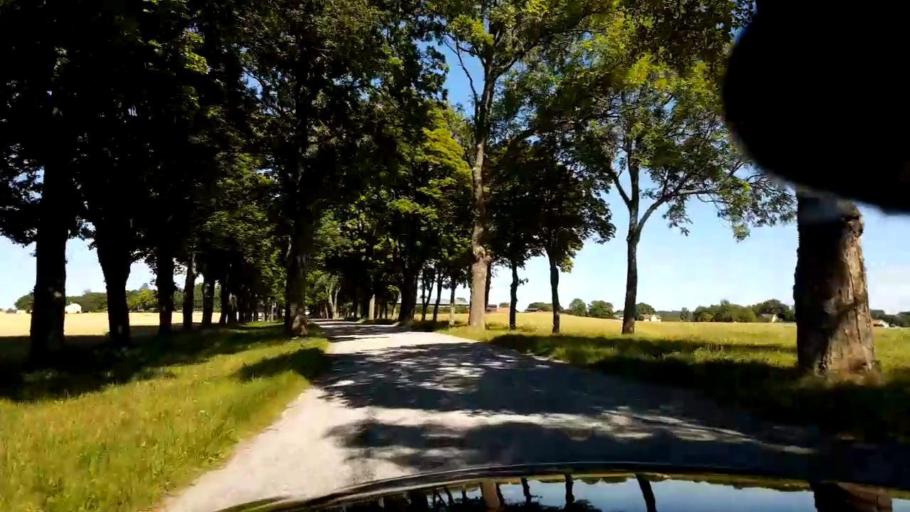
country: SE
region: Stockholm
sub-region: Sigtuna Kommun
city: Sigtuna
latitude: 59.6019
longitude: 17.6465
